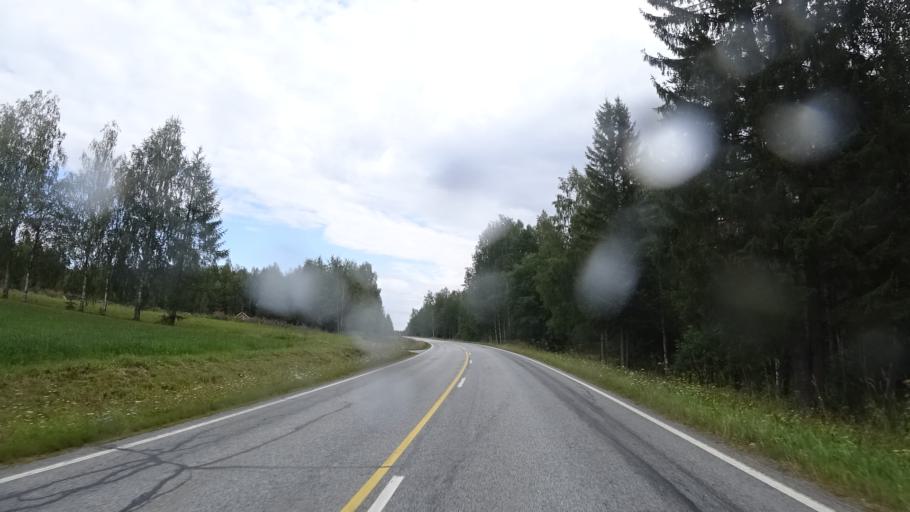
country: FI
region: North Karelia
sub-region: Keski-Karjala
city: Raeaekkylae
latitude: 62.1072
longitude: 29.7031
